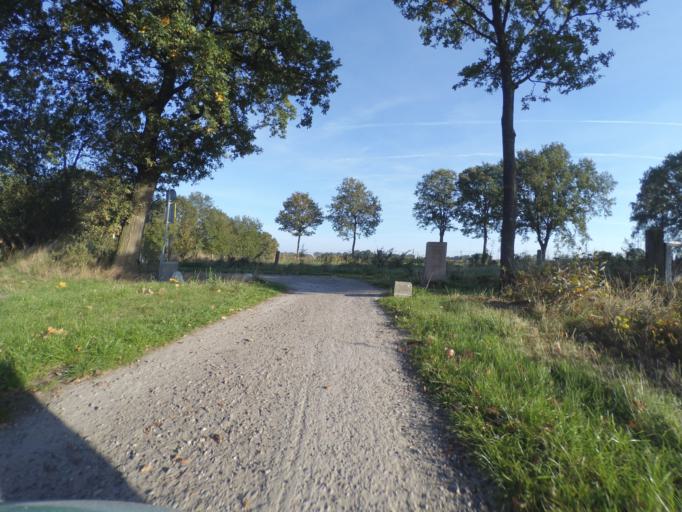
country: NL
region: Gelderland
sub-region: Gemeente Winterswijk
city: Winterswijk
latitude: 52.0388
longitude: 6.7181
